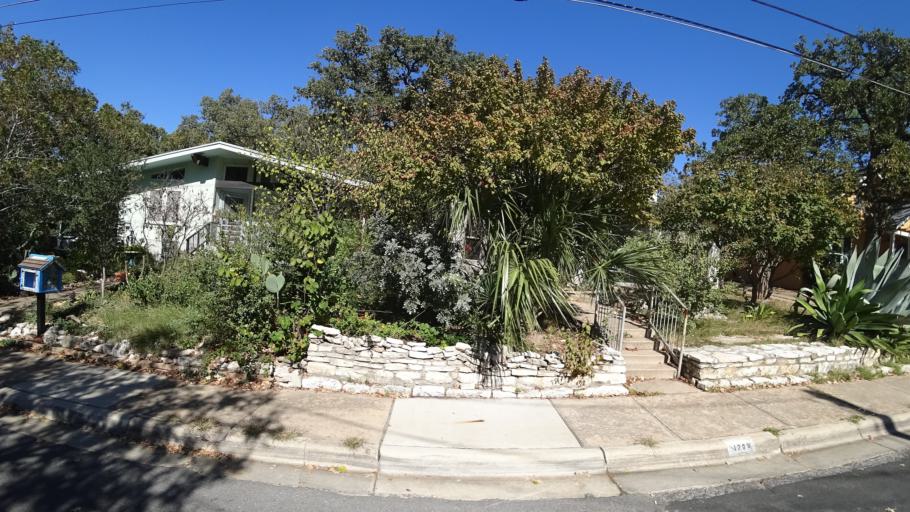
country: US
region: Texas
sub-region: Travis County
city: Austin
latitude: 30.2824
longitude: -97.7622
